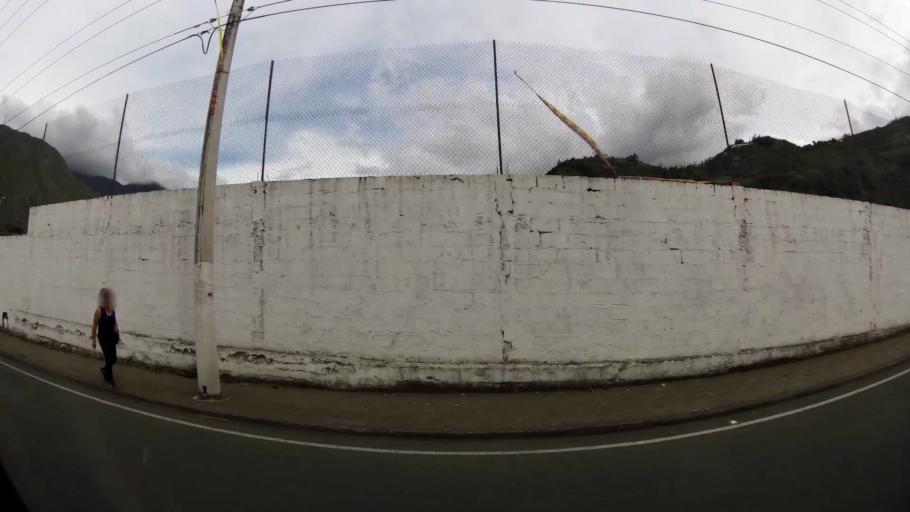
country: EC
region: Tungurahua
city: Banos
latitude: -1.3925
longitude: -78.4205
